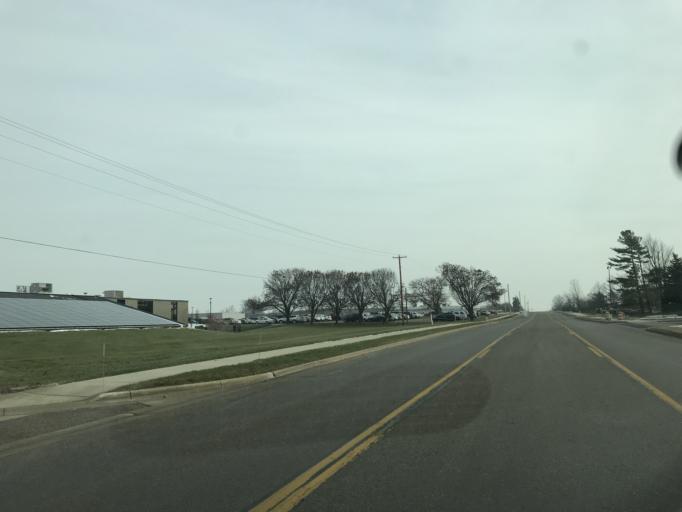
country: US
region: Michigan
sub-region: Ottawa County
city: Holland
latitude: 42.7621
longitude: -86.0758
